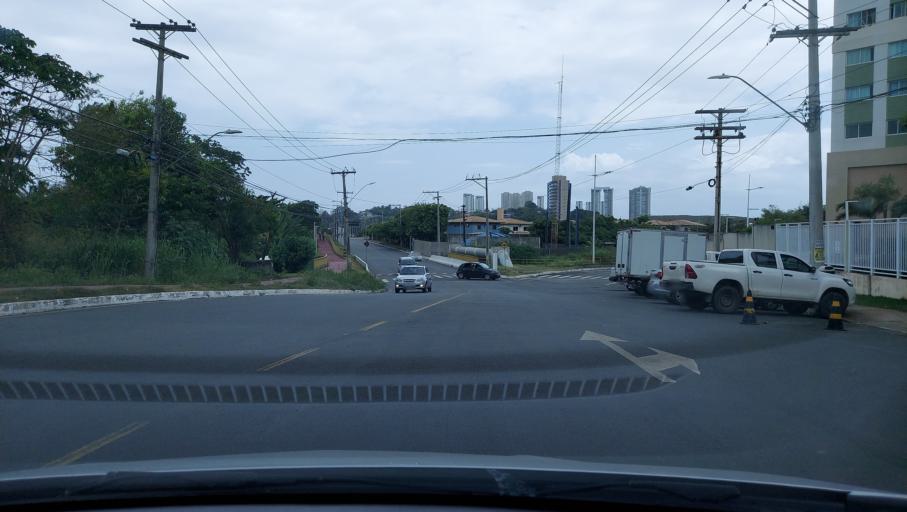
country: BR
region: Bahia
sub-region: Lauro De Freitas
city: Lauro de Freitas
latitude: -12.9503
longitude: -38.3888
